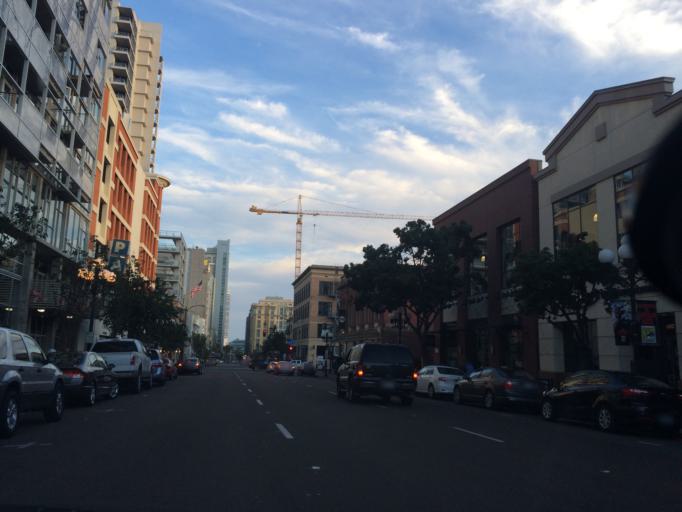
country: US
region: California
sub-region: San Diego County
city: San Diego
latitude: 32.7124
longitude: -117.1592
